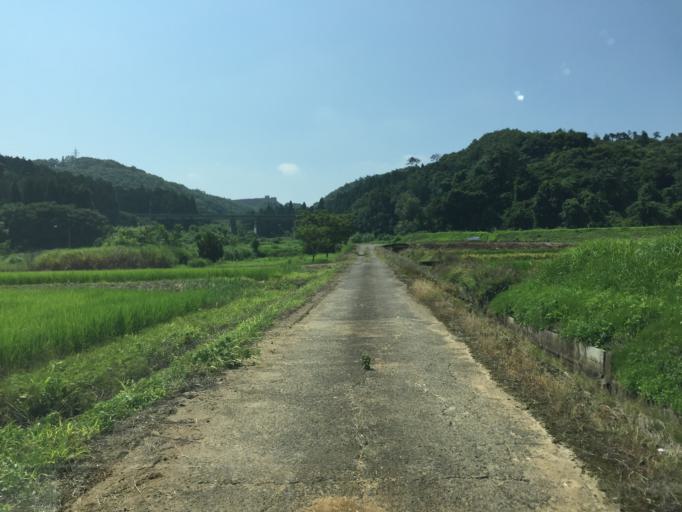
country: JP
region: Fukushima
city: Fukushima-shi
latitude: 37.7054
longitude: 140.4552
